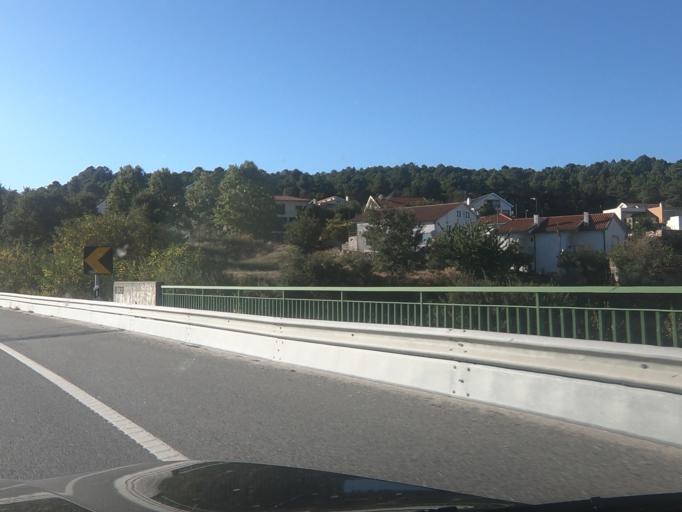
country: PT
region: Vila Real
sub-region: Vila Real
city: Vila Real
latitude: 41.3173
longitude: -7.7251
